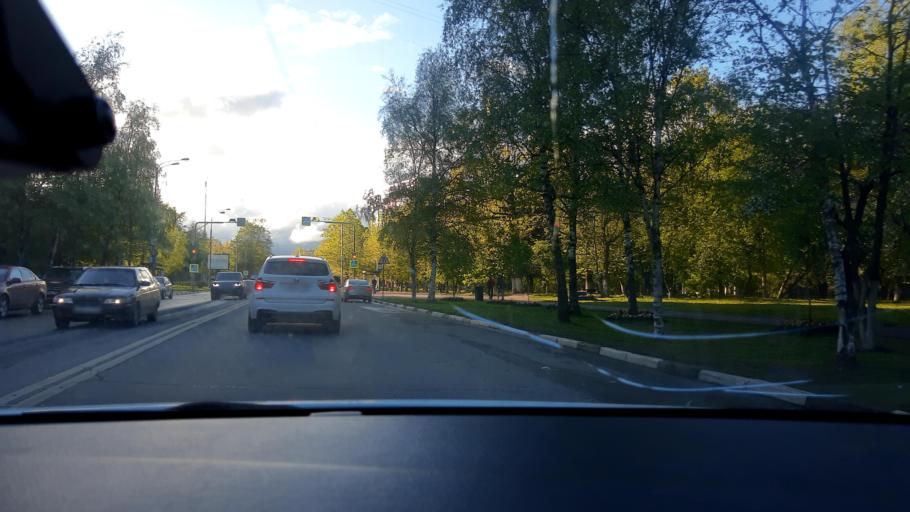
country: RU
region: Moskovskaya
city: Odintsovo
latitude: 55.6758
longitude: 37.2705
